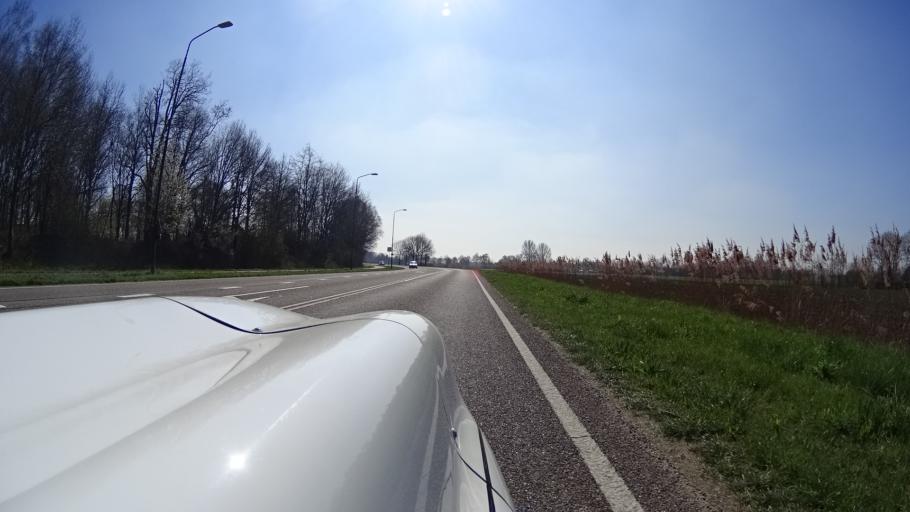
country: NL
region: North Brabant
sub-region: Gemeente Boekel
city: Boekel
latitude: 51.5528
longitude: 5.6730
